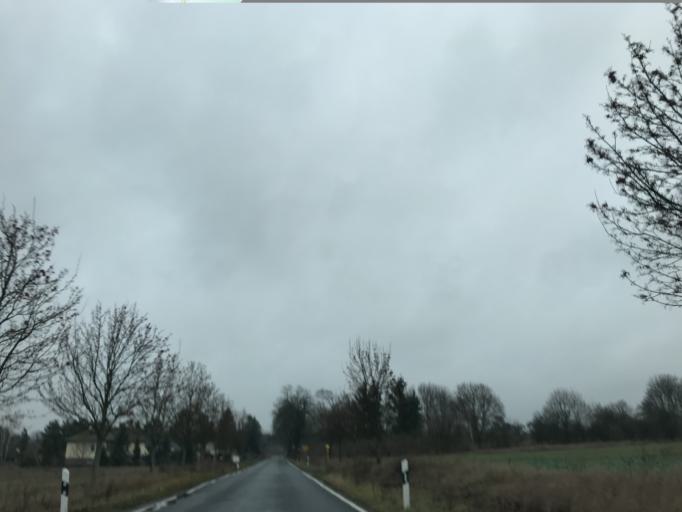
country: DE
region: Brandenburg
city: Brieselang
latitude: 52.6711
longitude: 12.9751
